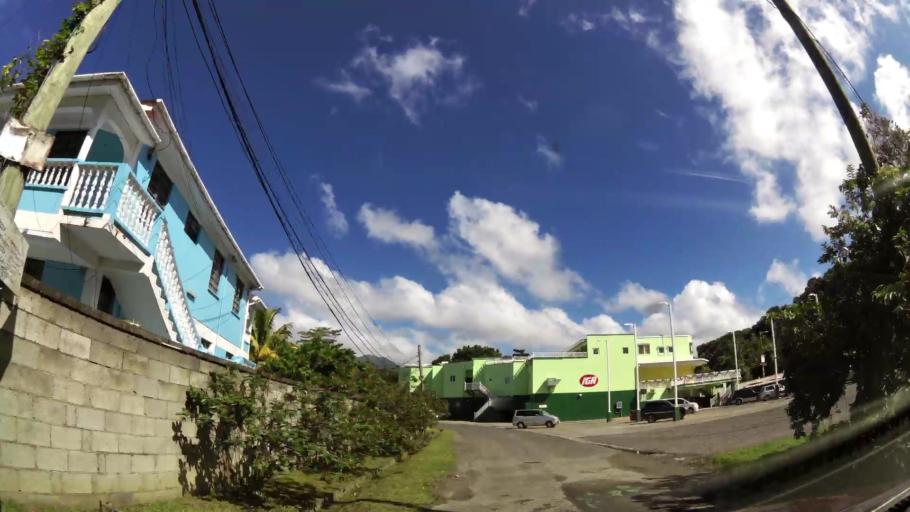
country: DM
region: Saint John
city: Portsmouth
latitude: 15.5586
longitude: -61.4574
